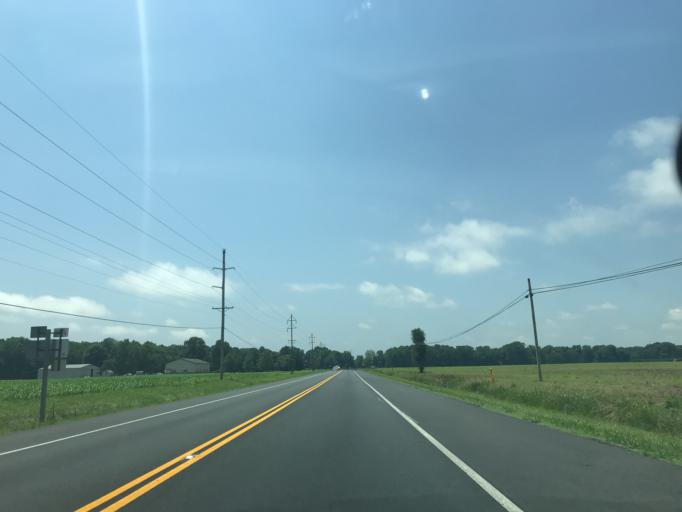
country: US
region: Maryland
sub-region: Dorchester County
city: Hurlock
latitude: 38.5916
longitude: -75.9368
